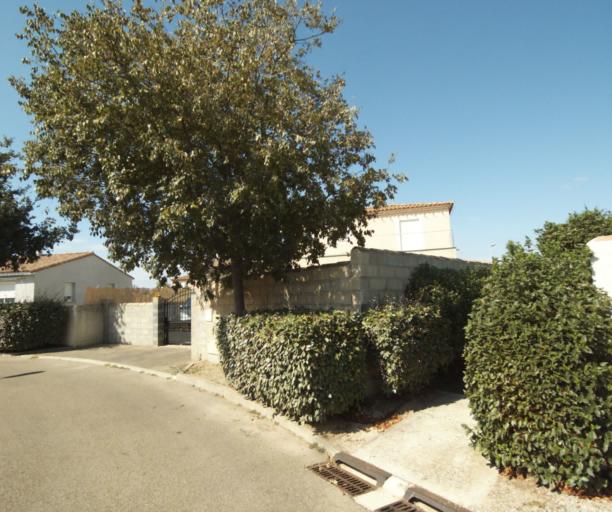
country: FR
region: Languedoc-Roussillon
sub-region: Departement du Gard
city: Bouillargues
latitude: 43.8049
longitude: 4.4342
